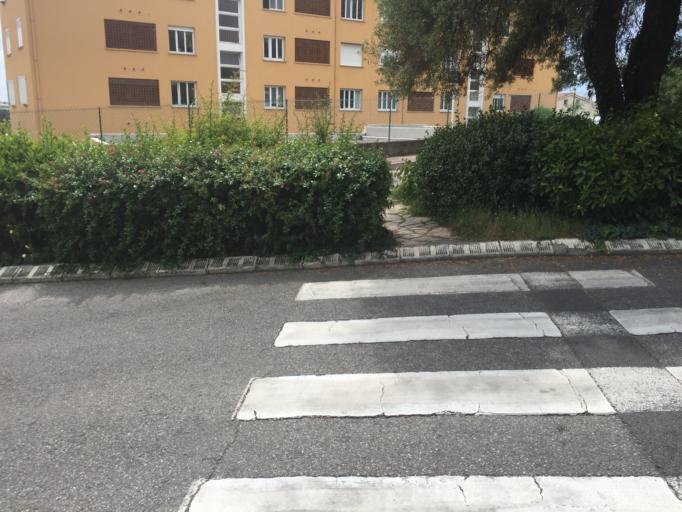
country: FR
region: Provence-Alpes-Cote d'Azur
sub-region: Departement des Alpes-Maritimes
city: Antibes
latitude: 43.5876
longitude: 7.1162
